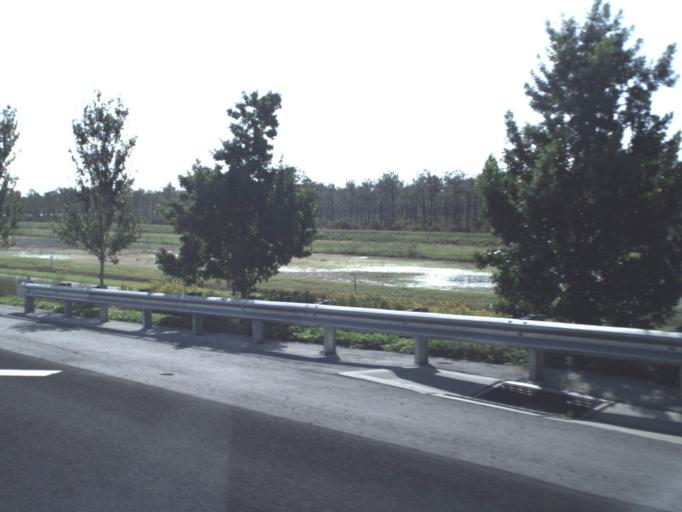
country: US
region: Florida
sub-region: Lee County
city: Three Oaks
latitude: 26.5117
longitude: -81.7922
